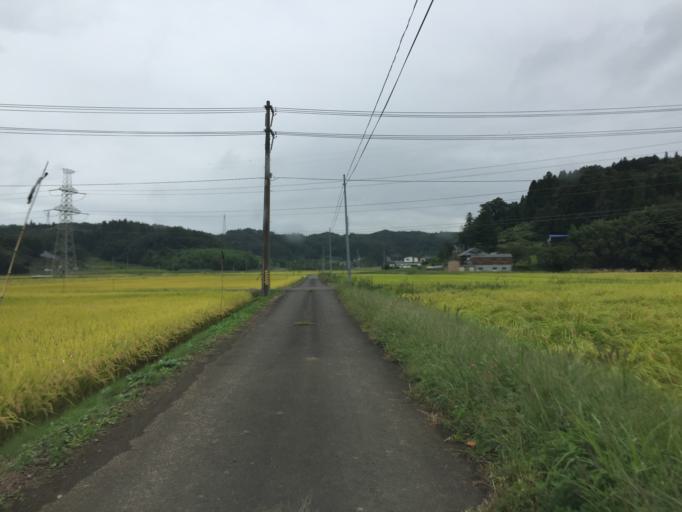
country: JP
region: Fukushima
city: Nihommatsu
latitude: 37.6503
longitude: 140.4447
